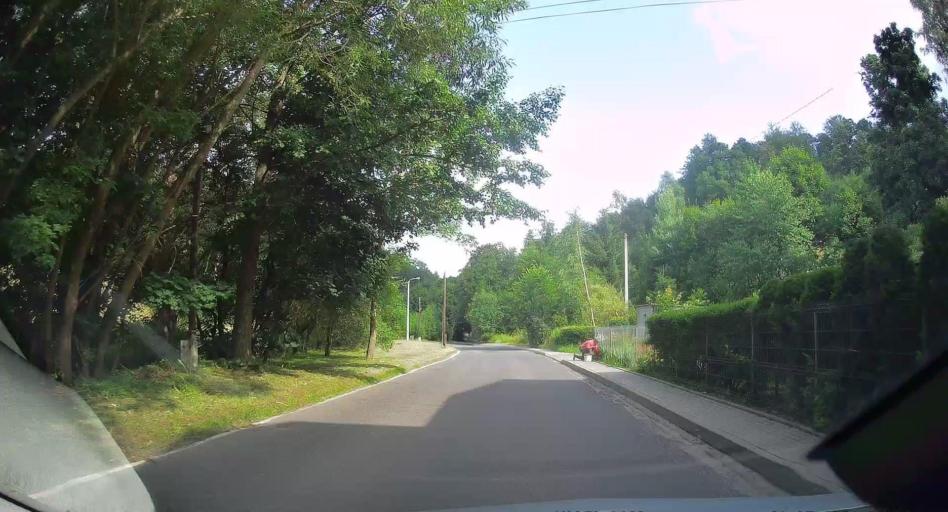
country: PL
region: Lower Silesian Voivodeship
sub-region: Powiat walbrzyski
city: Walim
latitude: 50.7070
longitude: 16.4371
